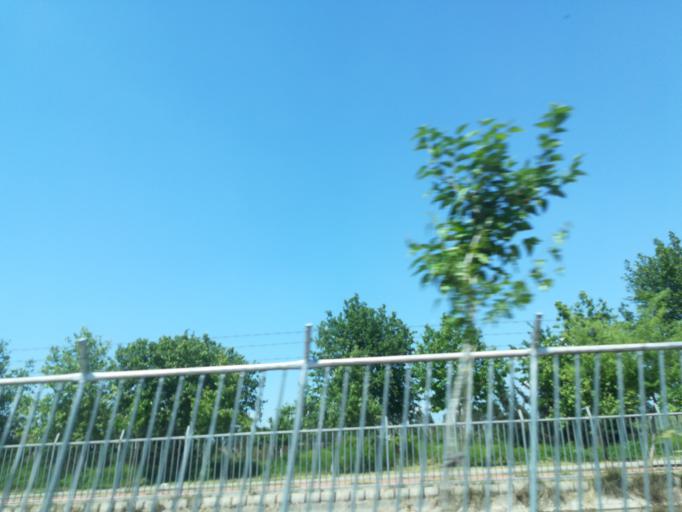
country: TR
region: Adana
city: Adana
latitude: 37.0239
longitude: 35.3674
